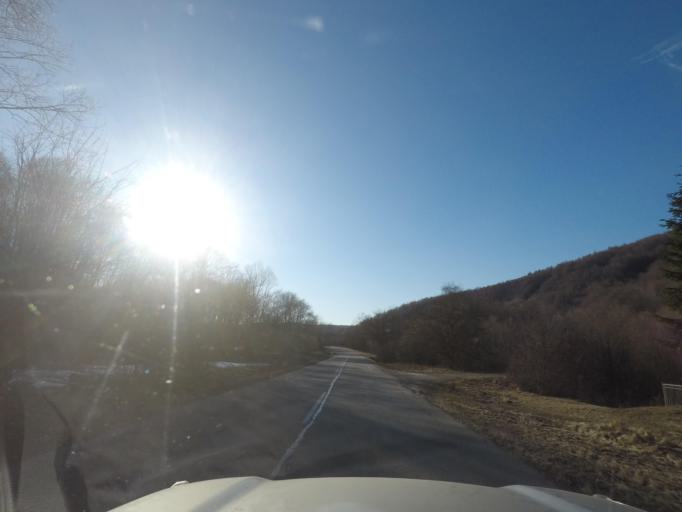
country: SK
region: Presovsky
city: Medzilaborce
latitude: 49.2811
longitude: 21.8346
